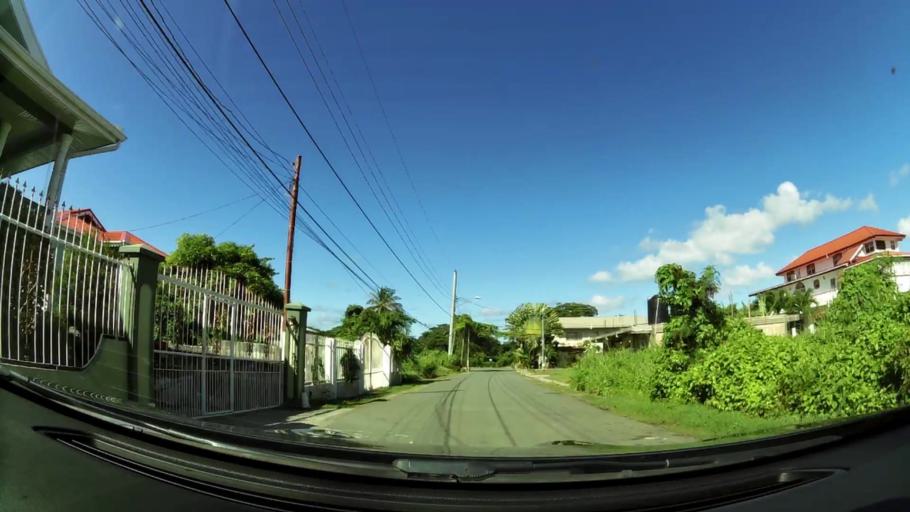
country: TT
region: Tobago
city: Scarborough
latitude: 11.1559
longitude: -60.7874
